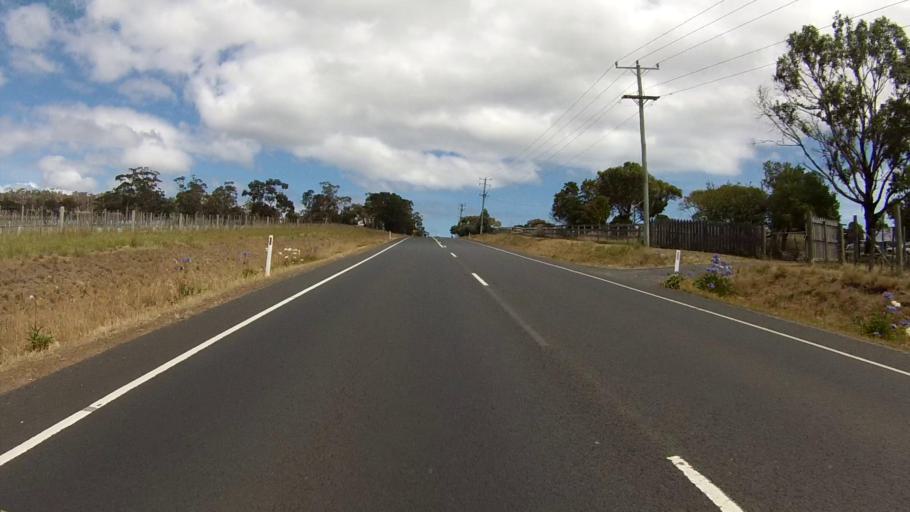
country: AU
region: Tasmania
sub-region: Sorell
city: Sorell
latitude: -42.8149
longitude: 147.6252
